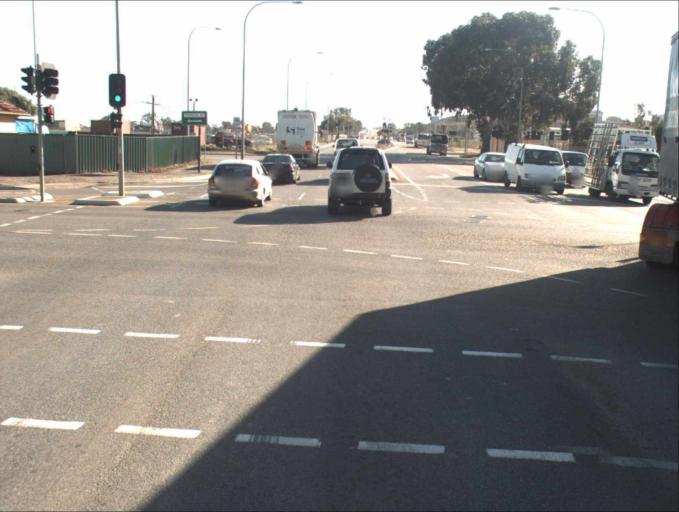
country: AU
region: South Australia
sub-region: Port Adelaide Enfield
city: Alberton
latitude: -34.8415
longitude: 138.5461
